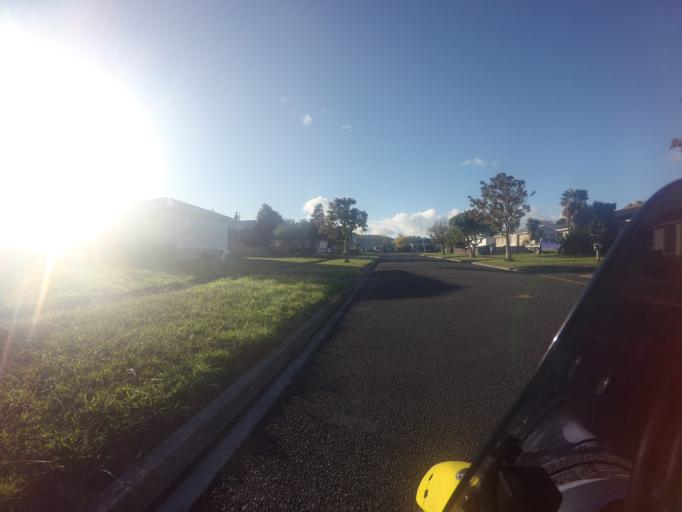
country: NZ
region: Gisborne
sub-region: Gisborne District
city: Gisborne
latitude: -38.6673
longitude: 178.0513
